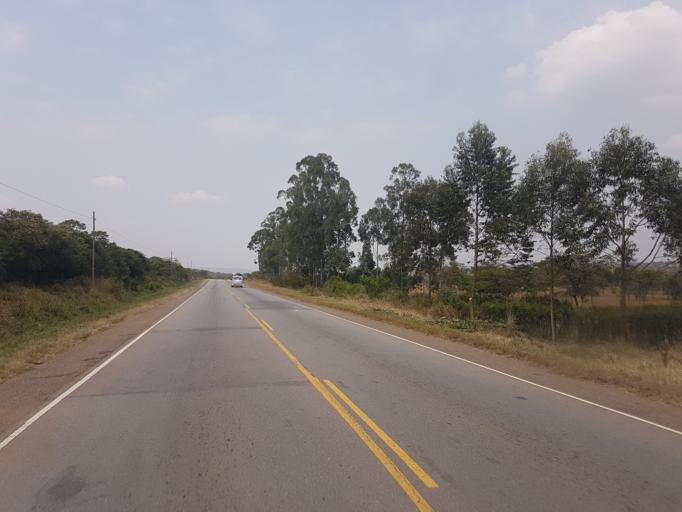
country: UG
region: Western Region
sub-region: Mbarara District
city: Mbarara
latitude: -0.5105
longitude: 30.7892
